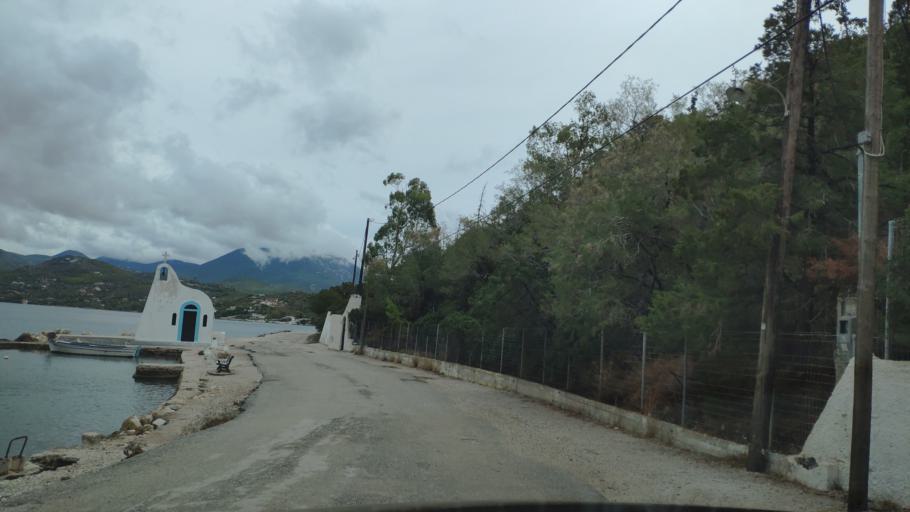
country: GR
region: Peloponnese
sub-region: Nomos Korinthias
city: Perachora
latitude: 38.0262
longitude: 22.8735
